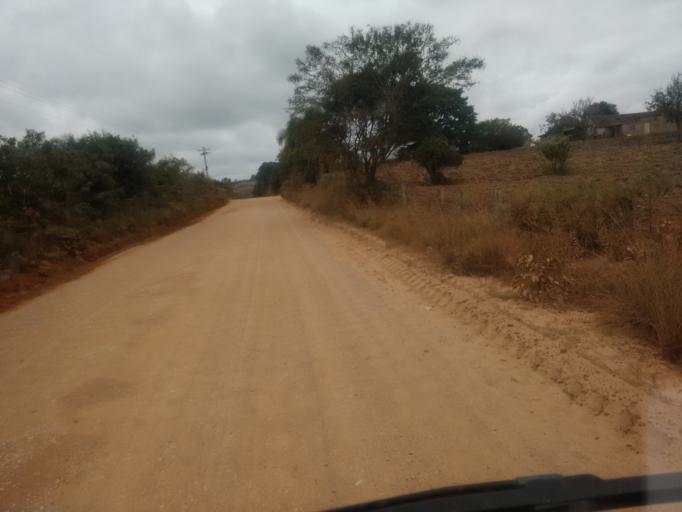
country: BR
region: Rio Grande do Sul
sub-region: Camaqua
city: Camaqua
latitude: -30.8123
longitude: -51.8203
